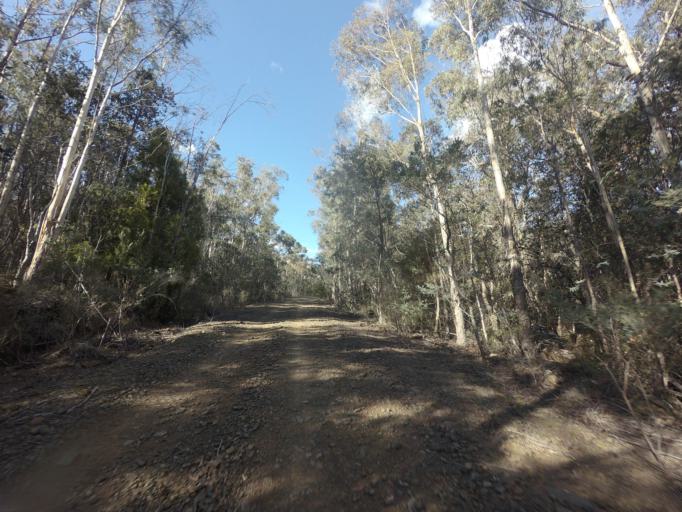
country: AU
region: Tasmania
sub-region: Break O'Day
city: St Helens
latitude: -41.8501
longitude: 148.0475
